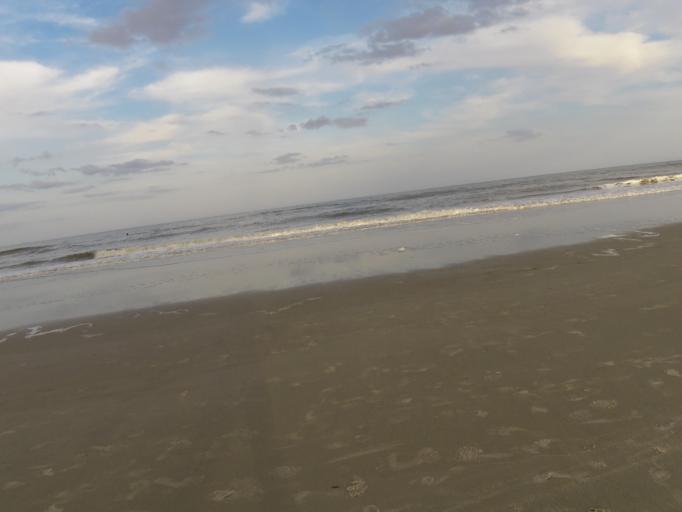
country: US
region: Florida
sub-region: Duval County
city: Jacksonville Beach
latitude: 30.3003
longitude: -81.3897
